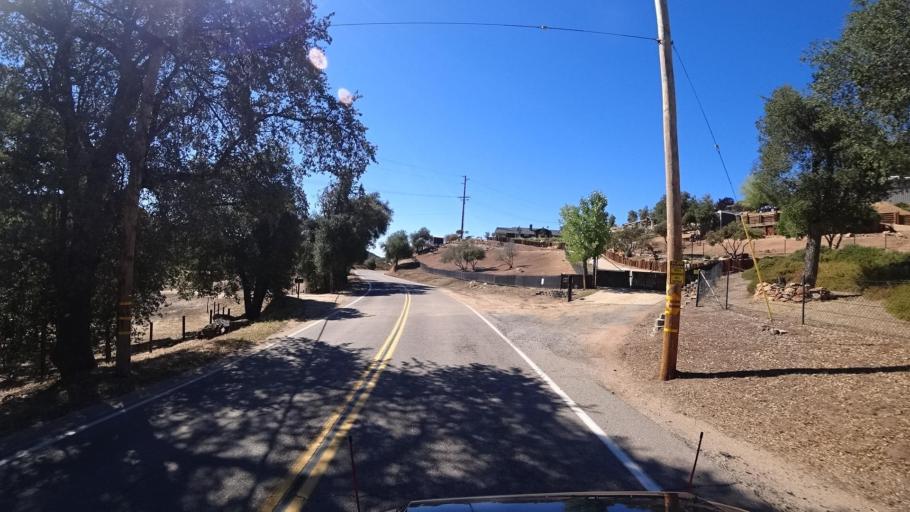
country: US
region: California
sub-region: San Diego County
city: Descanso
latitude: 32.8110
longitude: -116.6353
